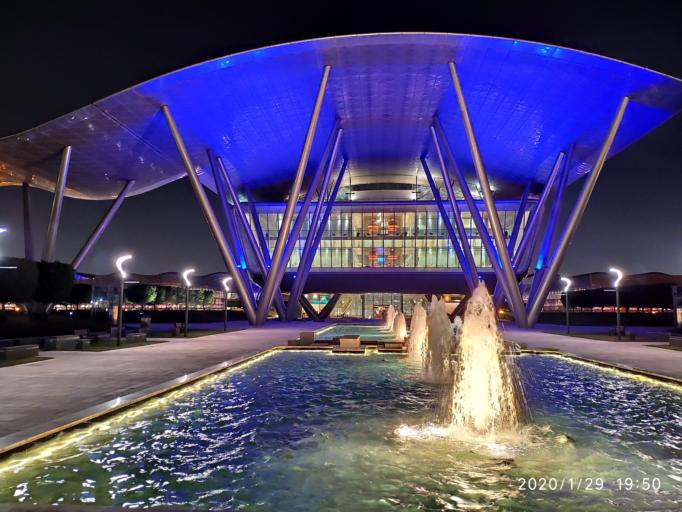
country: QA
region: Baladiyat ar Rayyan
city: Ar Rayyan
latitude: 25.3267
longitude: 51.4374
